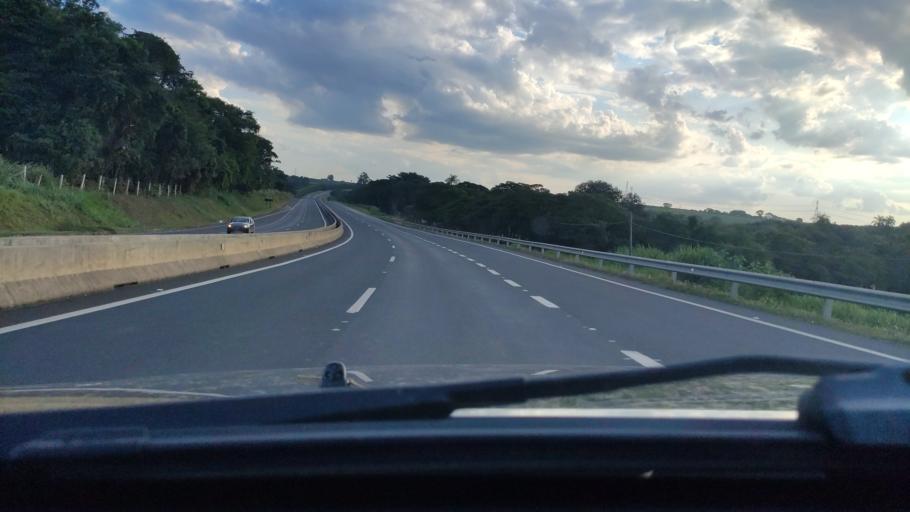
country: BR
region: Sao Paulo
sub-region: Mogi-Mirim
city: Mogi Mirim
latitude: -22.4425
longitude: -47.0514
